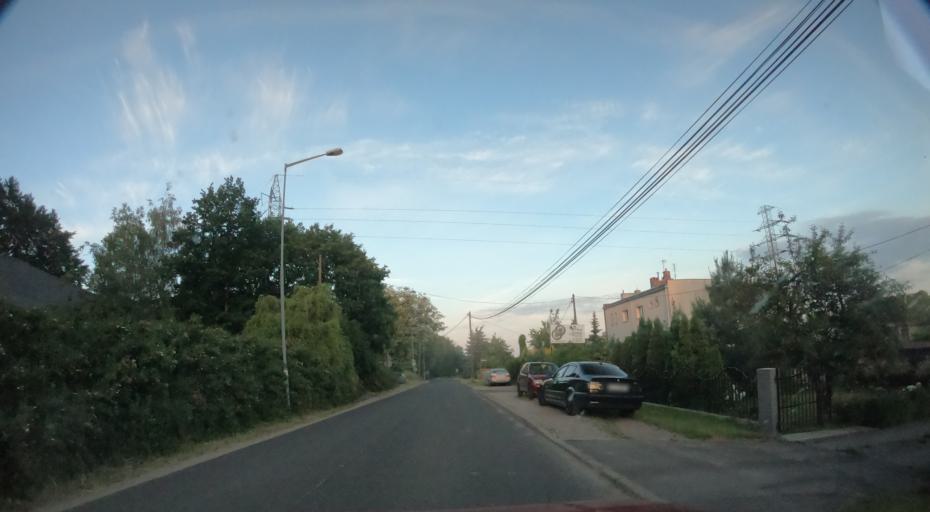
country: PL
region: Lubusz
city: Gorzow Wielkopolski
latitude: 52.7348
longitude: 15.2833
